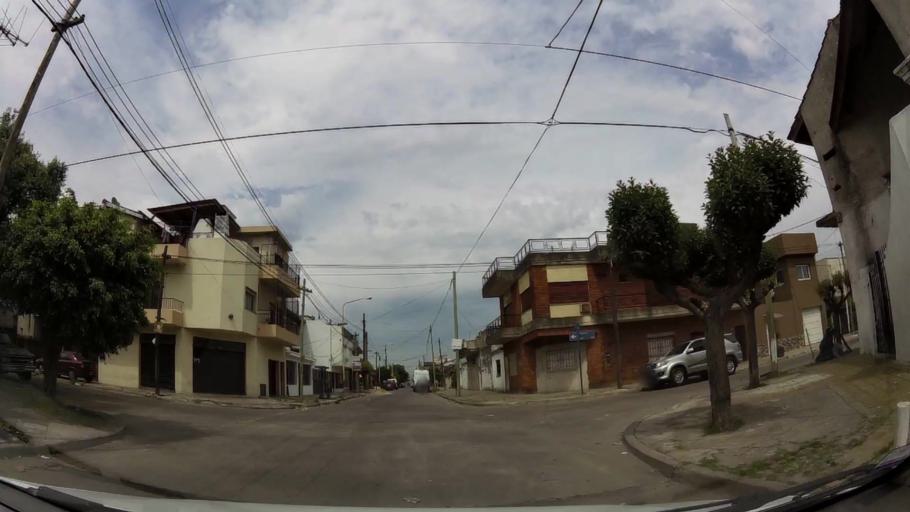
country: AR
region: Buenos Aires F.D.
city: Villa Lugano
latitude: -34.6869
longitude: -58.5039
